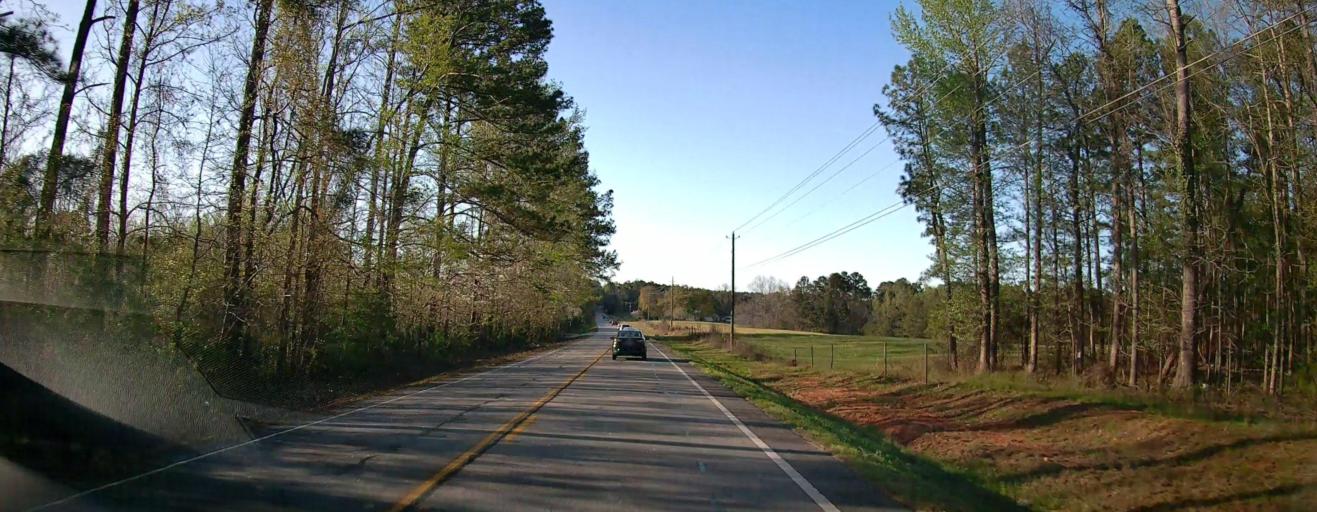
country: US
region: Georgia
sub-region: Newton County
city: Oakwood
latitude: 33.5025
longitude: -83.9198
